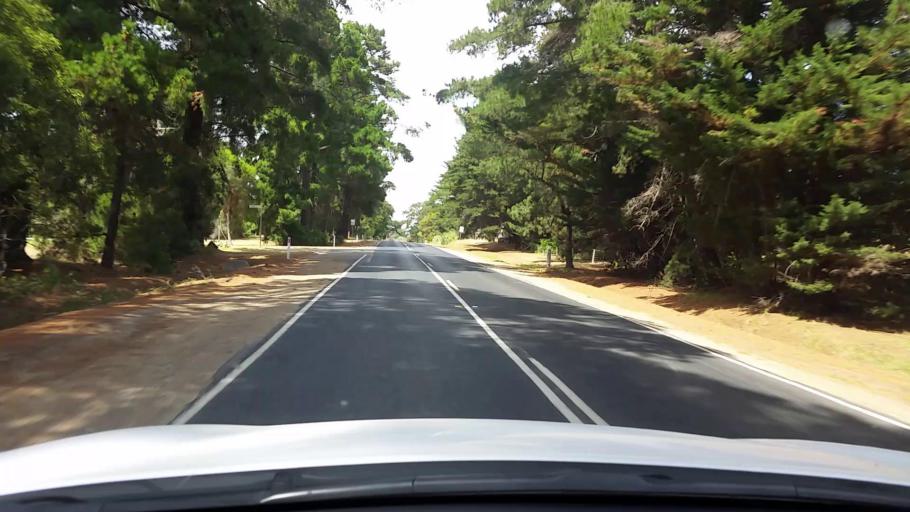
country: AU
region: Victoria
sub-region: Mornington Peninsula
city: Merricks
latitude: -38.4659
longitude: 145.0206
